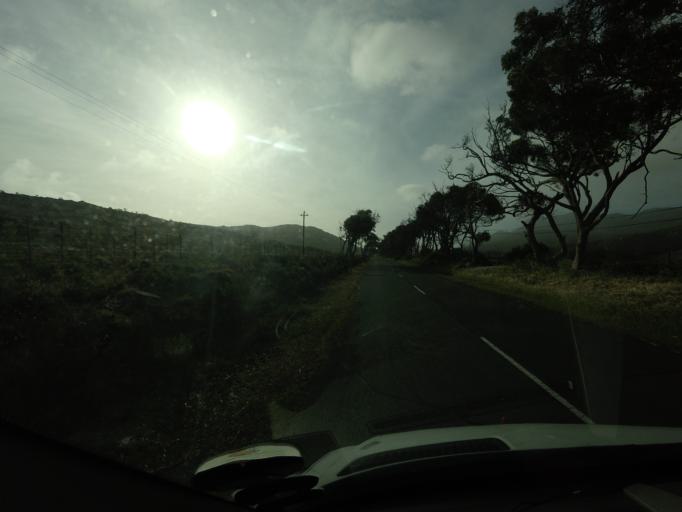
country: ZA
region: Western Cape
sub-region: City of Cape Town
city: Retreat
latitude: -34.2563
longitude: 18.4512
